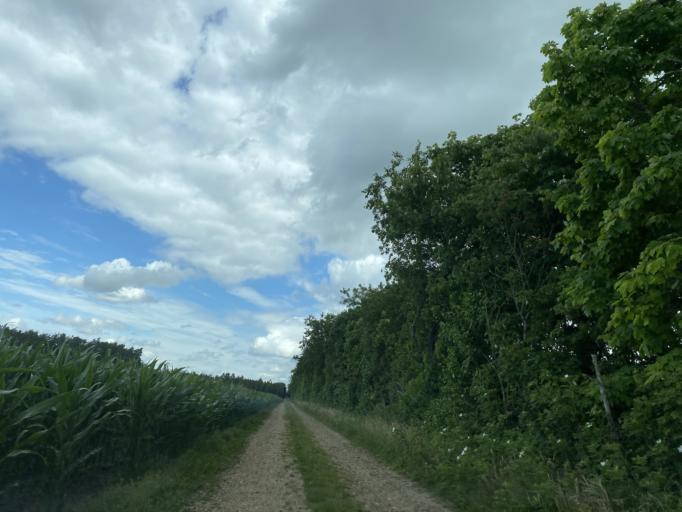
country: DK
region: Central Jutland
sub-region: Viborg Kommune
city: Bjerringbro
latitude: 56.2808
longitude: 9.6572
